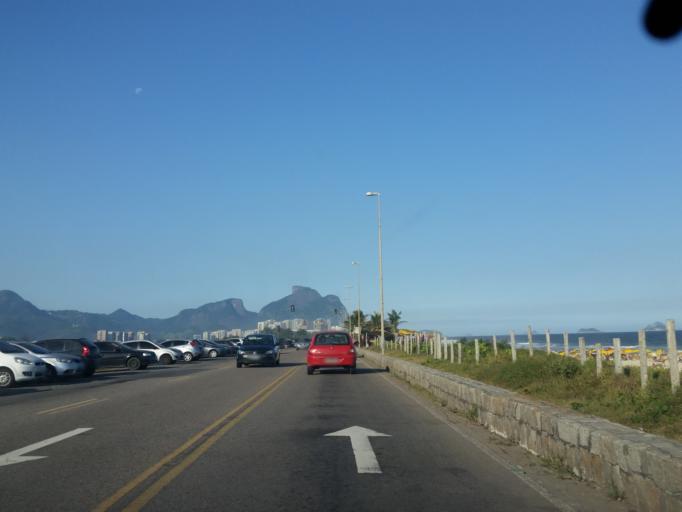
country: BR
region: Rio de Janeiro
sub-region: Nilopolis
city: Nilopolis
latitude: -23.0129
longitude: -43.3920
